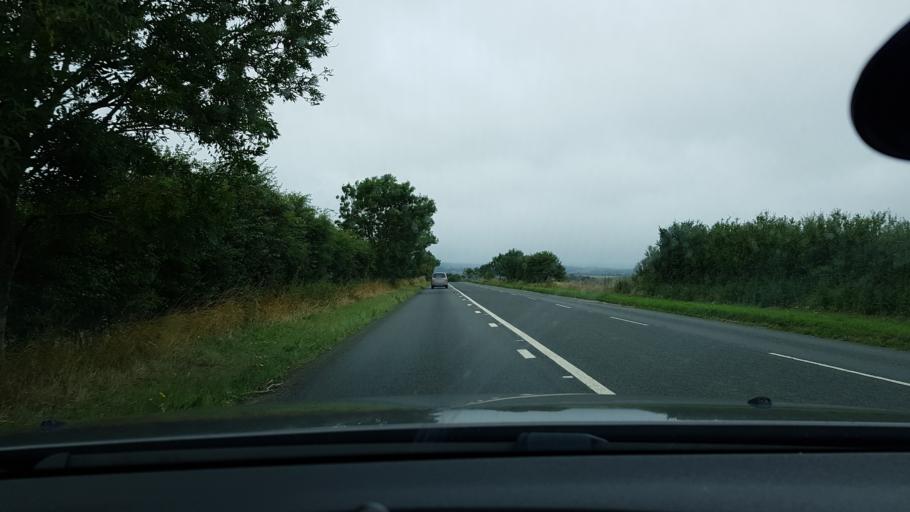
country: GB
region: England
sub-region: Wiltshire
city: Avebury
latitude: 51.4309
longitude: -1.9259
